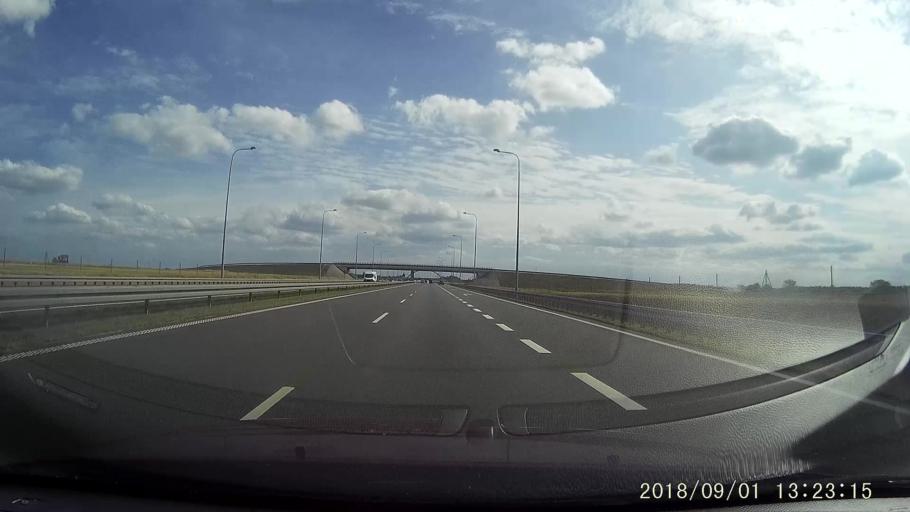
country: PL
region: West Pomeranian Voivodeship
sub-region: Powiat pyrzycki
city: Bielice
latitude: 53.1278
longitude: 14.7326
